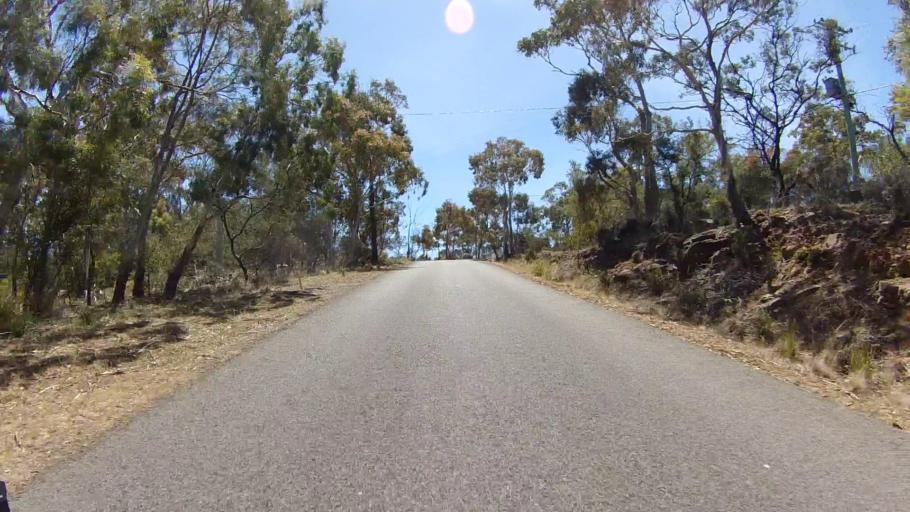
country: AU
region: Tasmania
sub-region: Clarence
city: Cambridge
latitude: -42.8485
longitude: 147.4313
